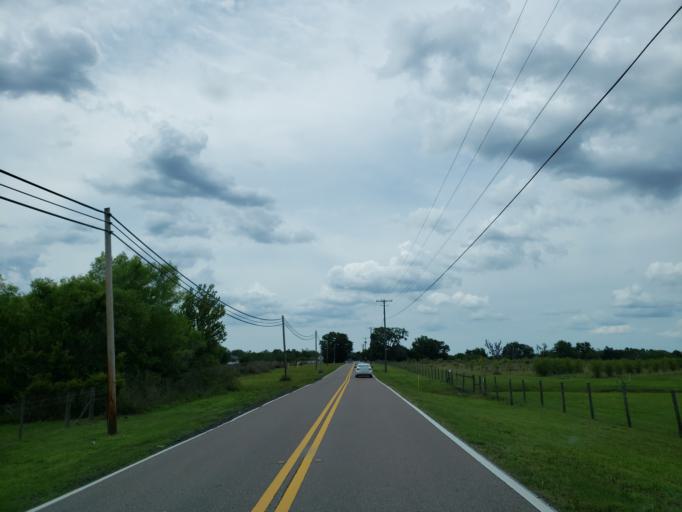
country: US
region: Florida
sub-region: Hillsborough County
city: Keystone
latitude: 28.1153
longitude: -82.6061
